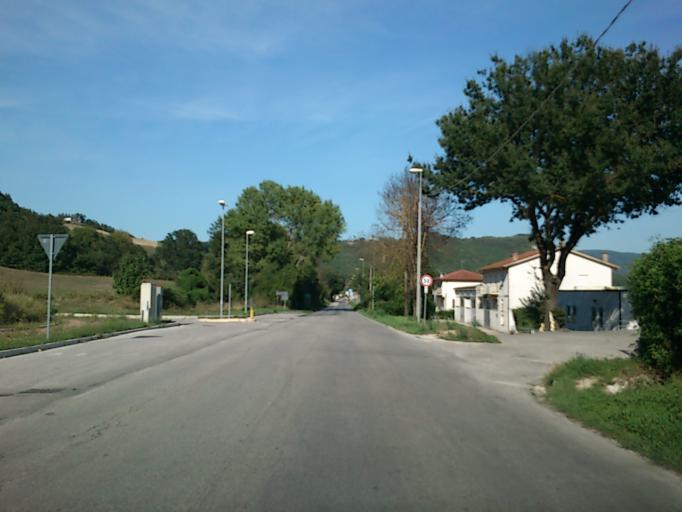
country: IT
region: The Marches
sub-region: Provincia di Pesaro e Urbino
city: Fermignano
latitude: 43.6951
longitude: 12.6493
